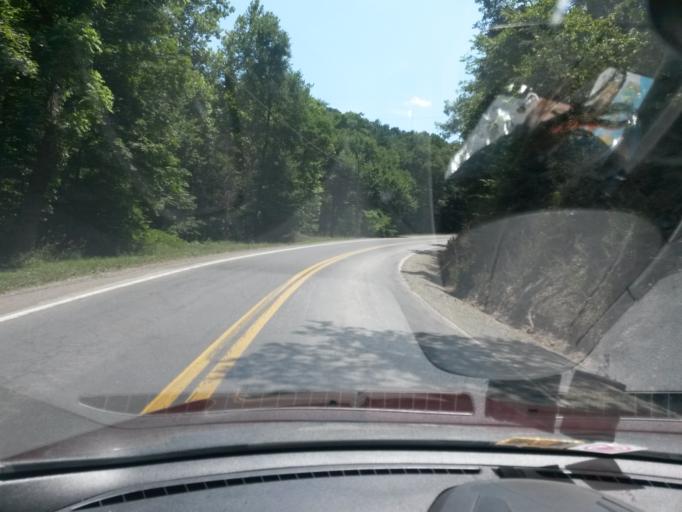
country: US
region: West Virginia
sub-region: Grant County
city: Petersburg
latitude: 38.9717
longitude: -79.1417
